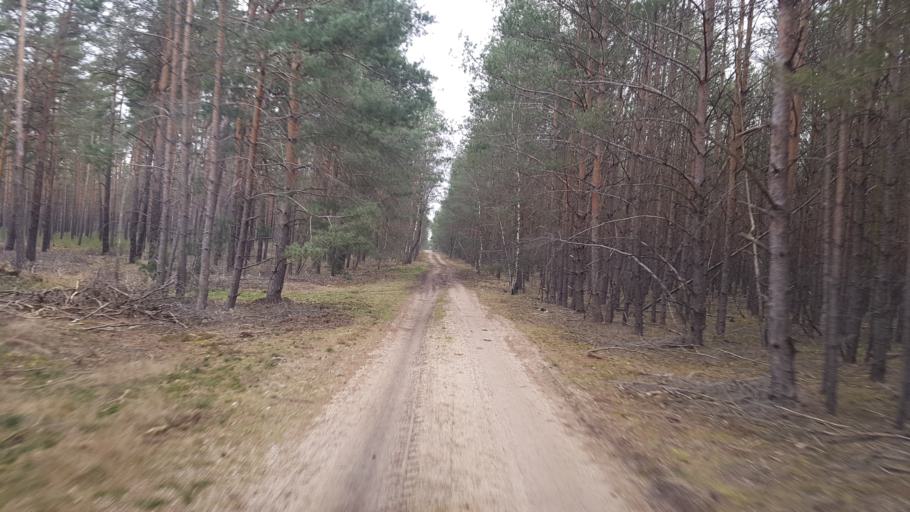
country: DE
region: Brandenburg
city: Schilda
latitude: 51.6254
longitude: 13.3853
